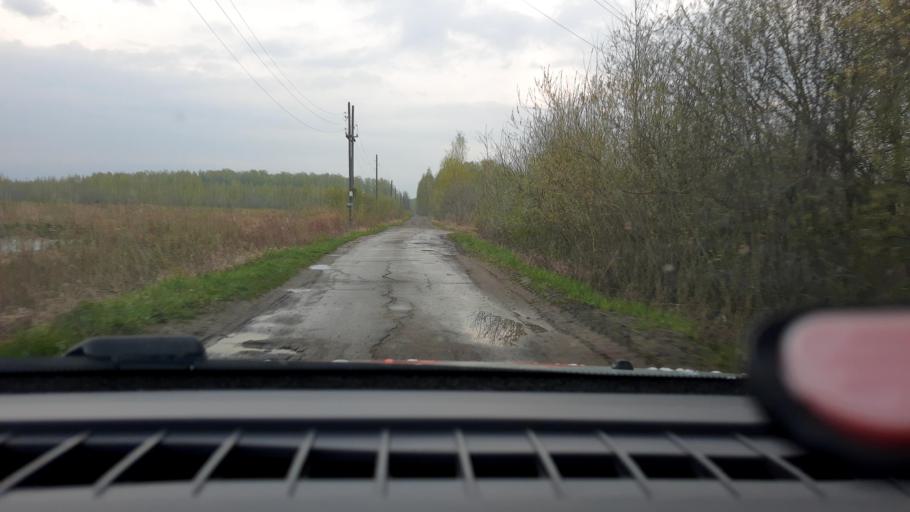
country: RU
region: Nizjnij Novgorod
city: Gorbatovka
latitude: 56.3058
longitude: 43.7694
